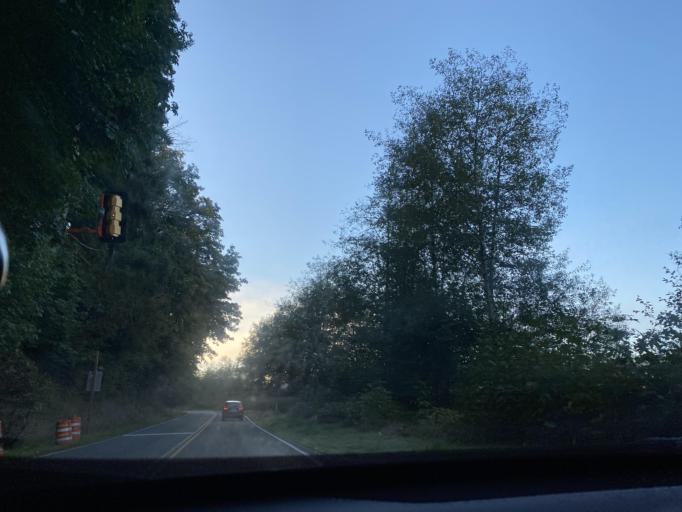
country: US
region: Washington
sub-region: Clallam County
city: Forks
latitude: 47.8205
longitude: -124.1795
